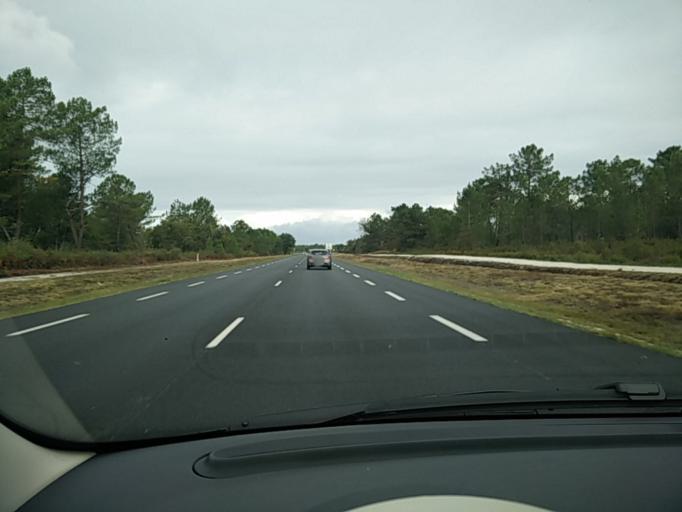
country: FR
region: Aquitaine
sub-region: Departement de la Gironde
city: Lacanau
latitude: 44.9872
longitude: -1.0726
